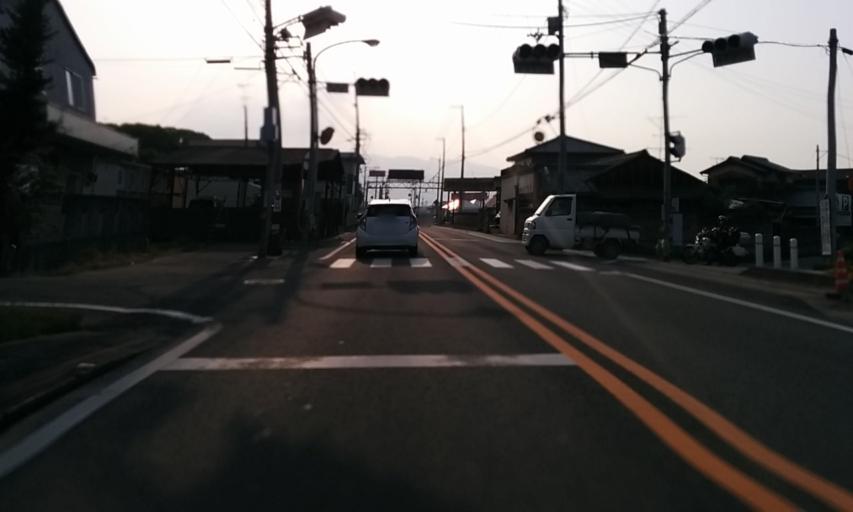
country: JP
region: Ehime
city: Saijo
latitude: 33.8961
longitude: 133.1249
